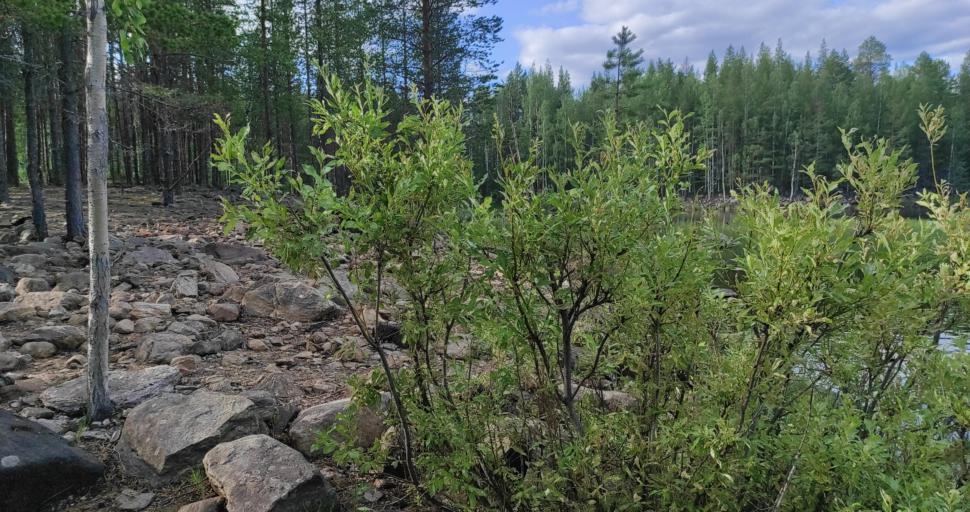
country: RU
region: Murmansk
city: Zelenoborskiy
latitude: 66.6888
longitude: 32.5234
